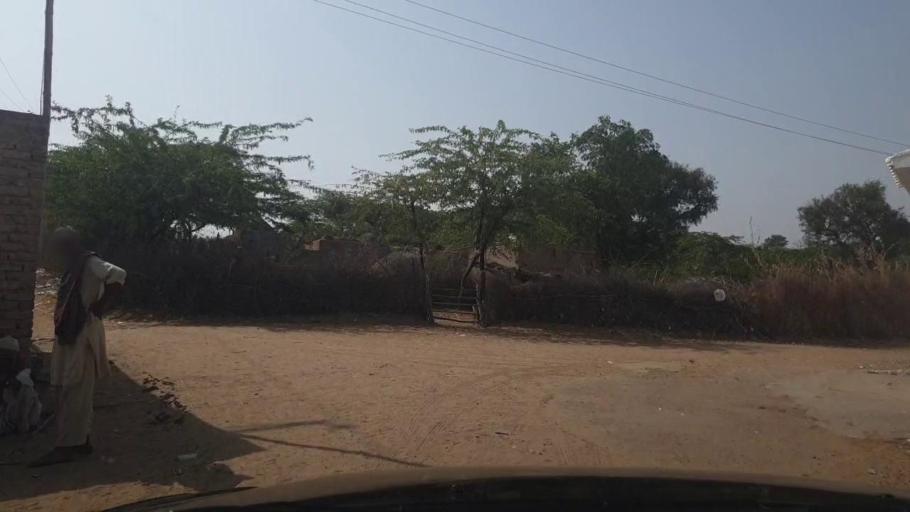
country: PK
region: Sindh
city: Islamkot
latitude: 24.9956
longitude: 70.2047
